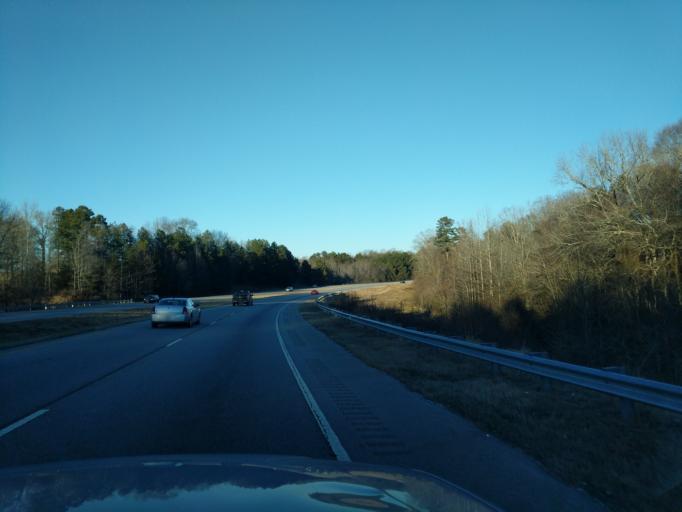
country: US
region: Georgia
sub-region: Stephens County
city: Toccoa
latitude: 34.5393
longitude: -83.2958
